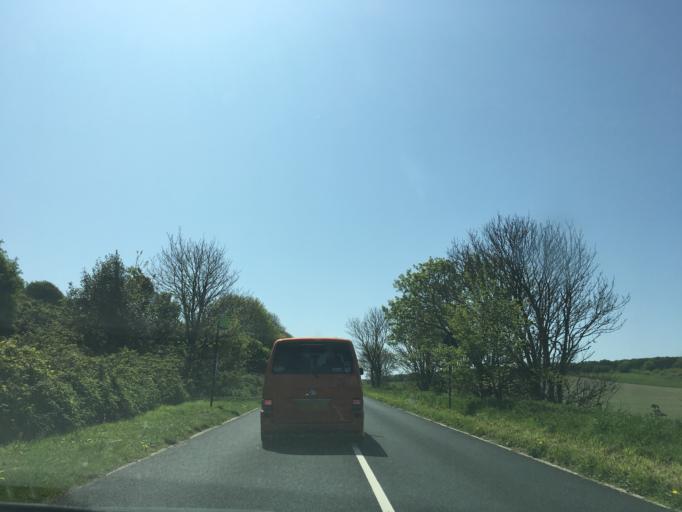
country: GB
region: England
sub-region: Isle of Wight
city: Niton
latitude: 50.5866
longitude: -1.2915
